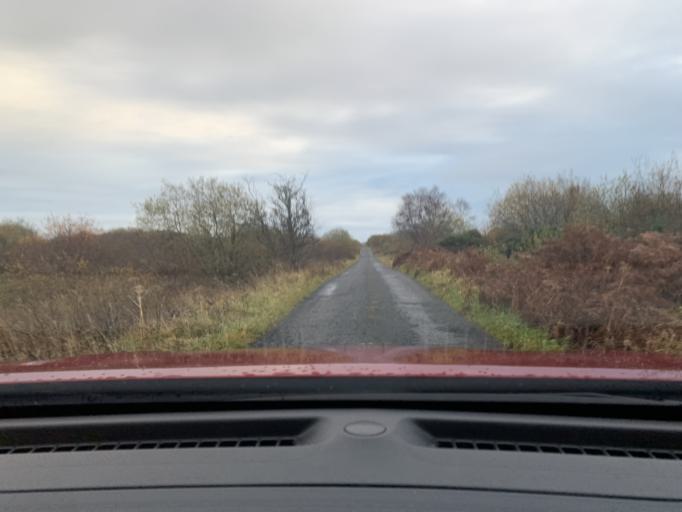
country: IE
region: Connaught
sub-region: Sligo
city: Ballymote
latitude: 54.0166
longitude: -8.5132
